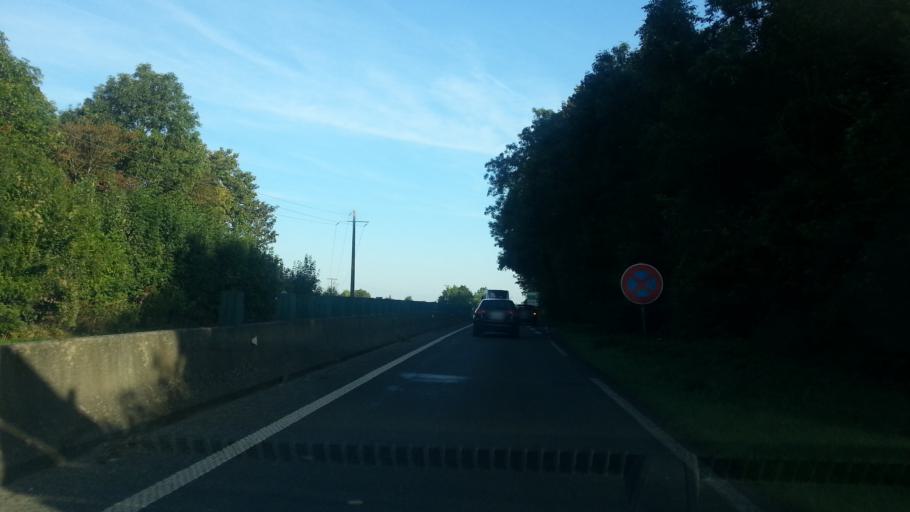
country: FR
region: Picardie
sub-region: Departement de l'Oise
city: Beauvais
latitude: 49.4571
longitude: 2.0677
